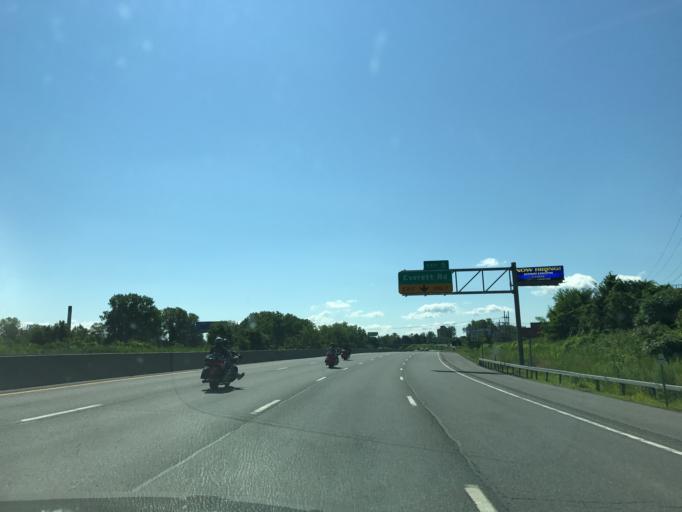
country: US
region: New York
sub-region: Albany County
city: West Albany
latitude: 42.6860
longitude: -73.7920
